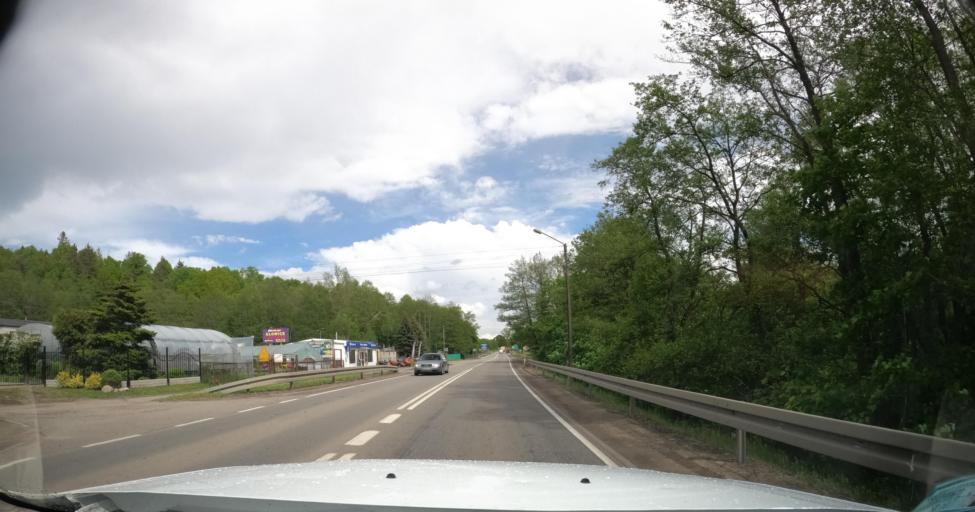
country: PL
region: Pomeranian Voivodeship
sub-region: Powiat kartuski
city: Zukowo
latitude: 54.3389
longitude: 18.3939
